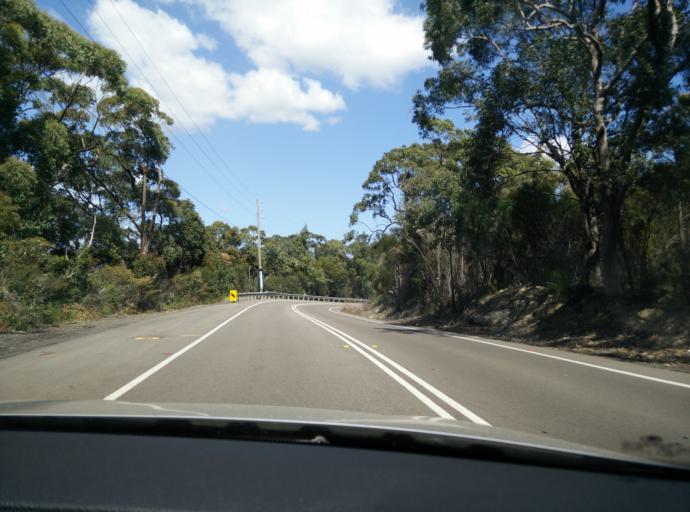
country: AU
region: New South Wales
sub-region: Gosford Shire
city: Blackwall
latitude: -33.4868
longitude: 151.3038
